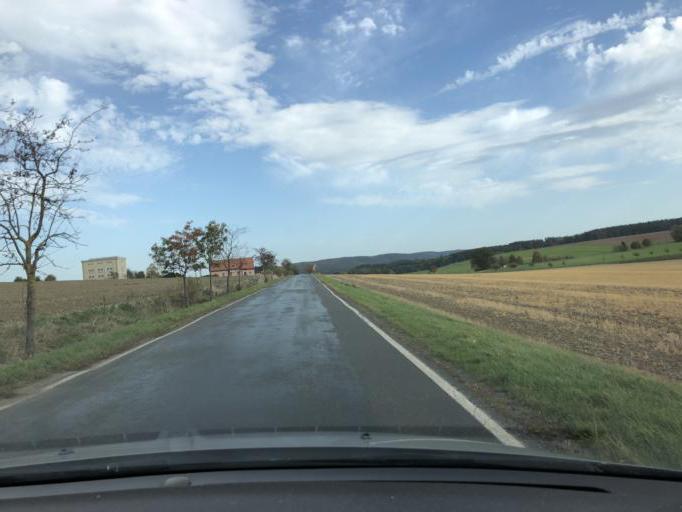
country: DE
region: Thuringia
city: Tonndorf
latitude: 50.8917
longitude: 11.2308
